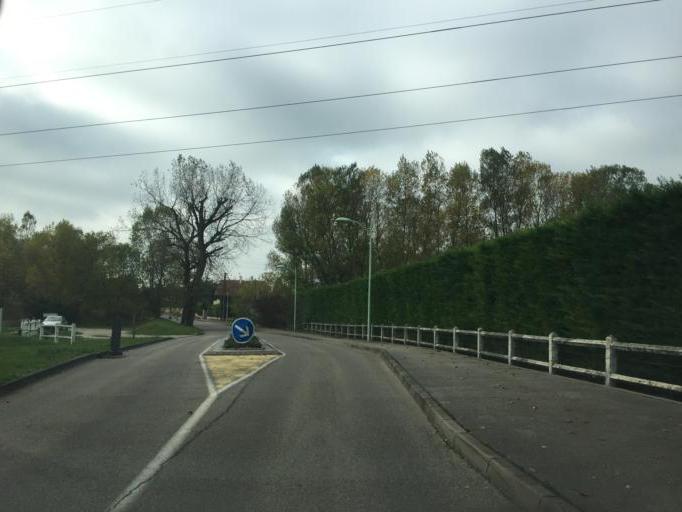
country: FR
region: Rhone-Alpes
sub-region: Departement de l'Ain
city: Thil
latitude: 45.8140
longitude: 5.0314
